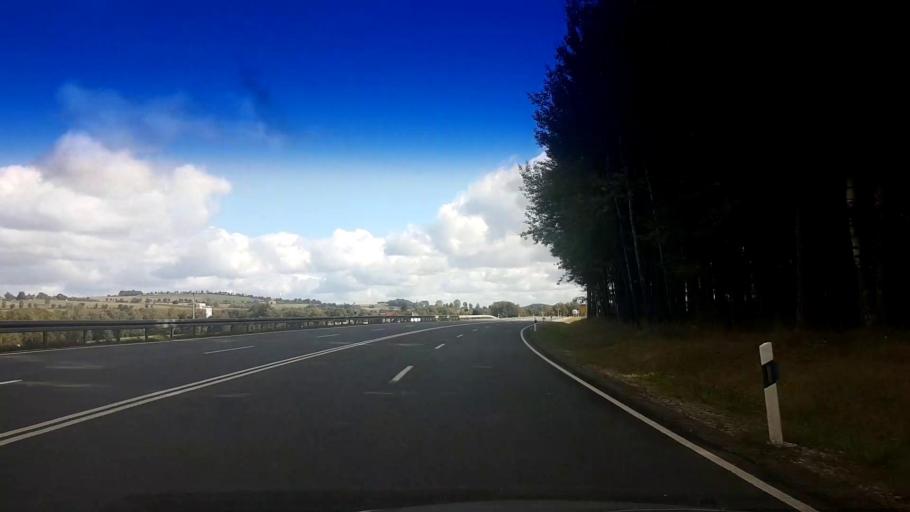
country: DE
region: Bavaria
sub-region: Upper Franconia
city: Trostau
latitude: 50.0166
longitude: 11.9290
